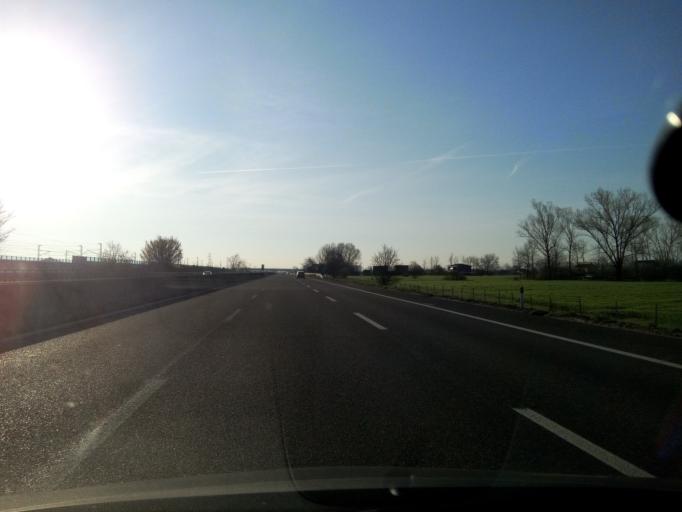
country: IT
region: Emilia-Romagna
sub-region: Provincia di Piacenza
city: Alseno
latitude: 44.9117
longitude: 10.0165
